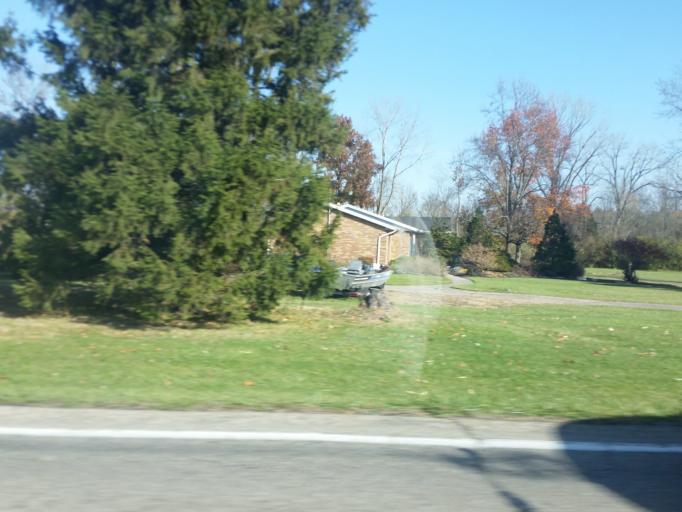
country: US
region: Ohio
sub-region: Butler County
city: Oxford
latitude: 39.4734
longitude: -84.7066
